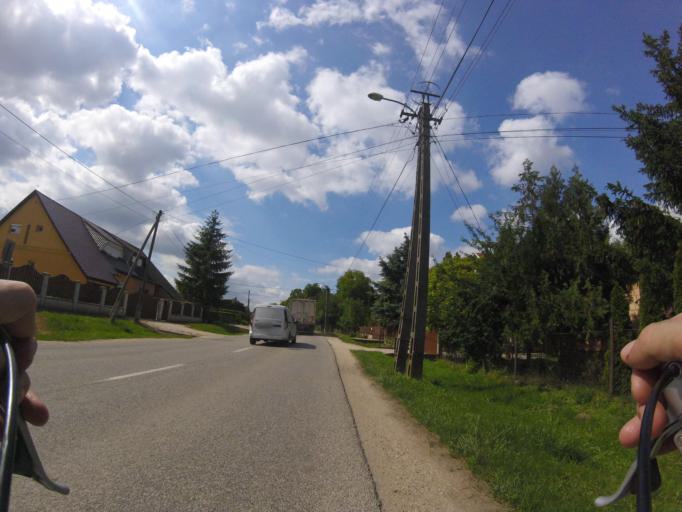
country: HU
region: Fejer
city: Szabadbattyan
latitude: 47.0828
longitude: 18.4074
